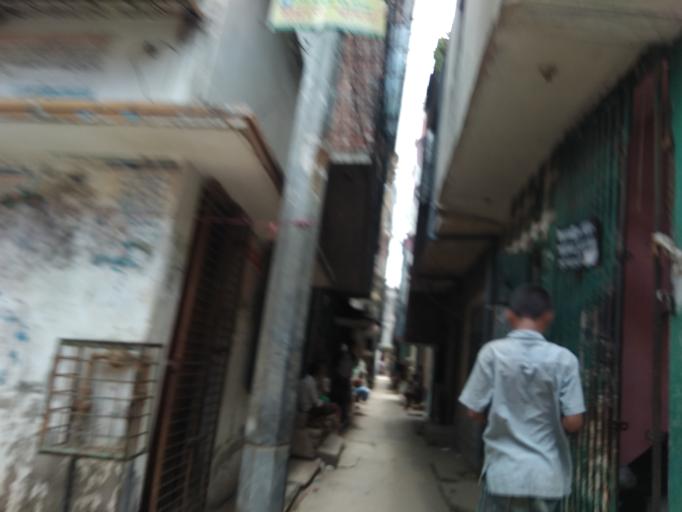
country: BD
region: Dhaka
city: Tungi
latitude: 23.8286
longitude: 90.3727
